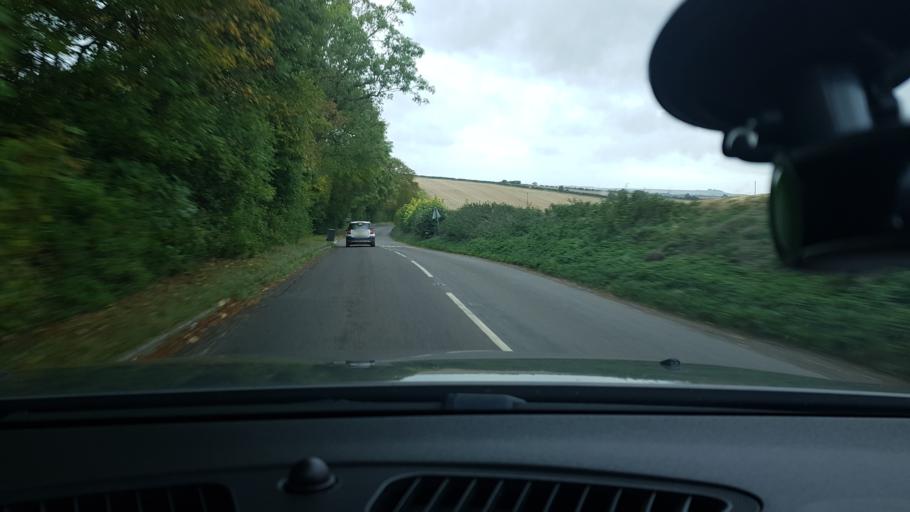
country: GB
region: England
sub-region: Wiltshire
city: Shalbourne
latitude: 51.3581
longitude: -1.5724
